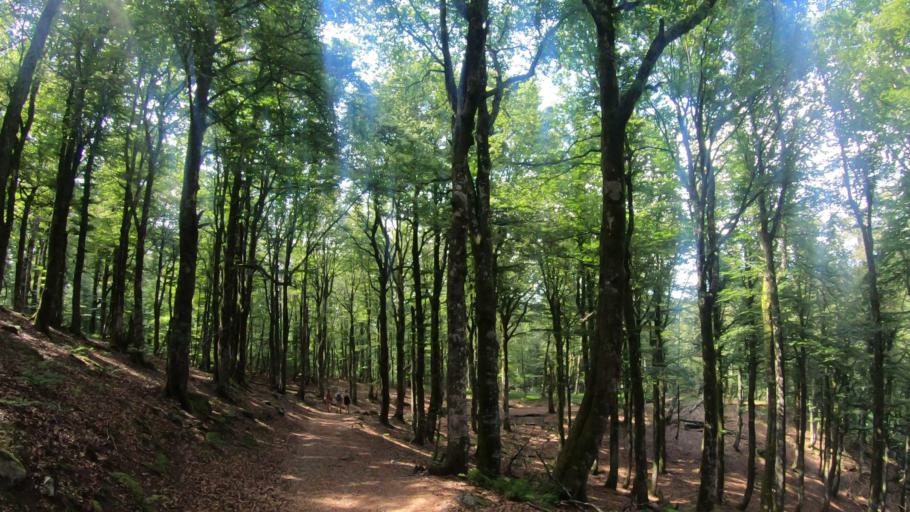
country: FR
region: Alsace
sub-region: Departement du Haut-Rhin
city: Metzeral
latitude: 48.0618
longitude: 7.0243
